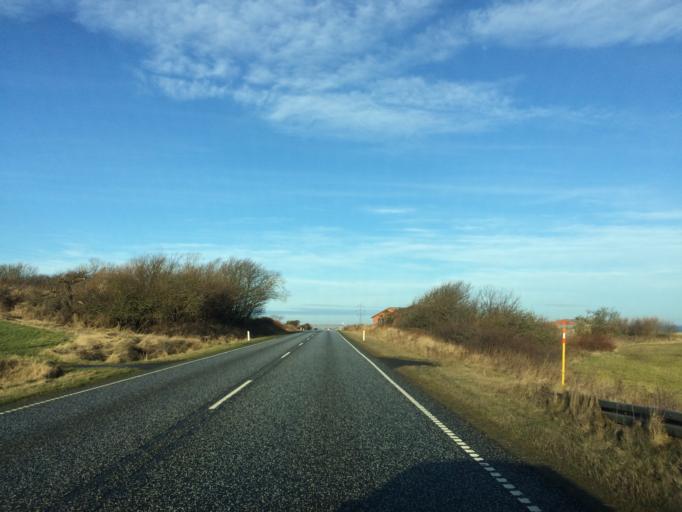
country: DK
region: Central Jutland
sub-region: Struer Kommune
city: Struer
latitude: 56.5528
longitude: 8.5583
